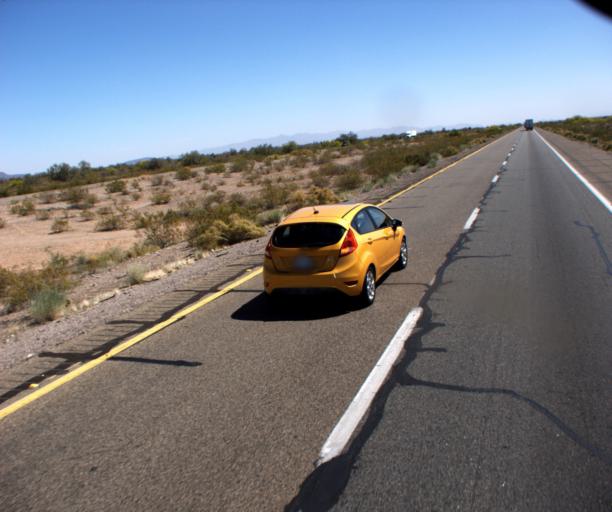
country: US
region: Arizona
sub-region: Maricopa County
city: Buckeye
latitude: 33.5092
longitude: -113.0041
